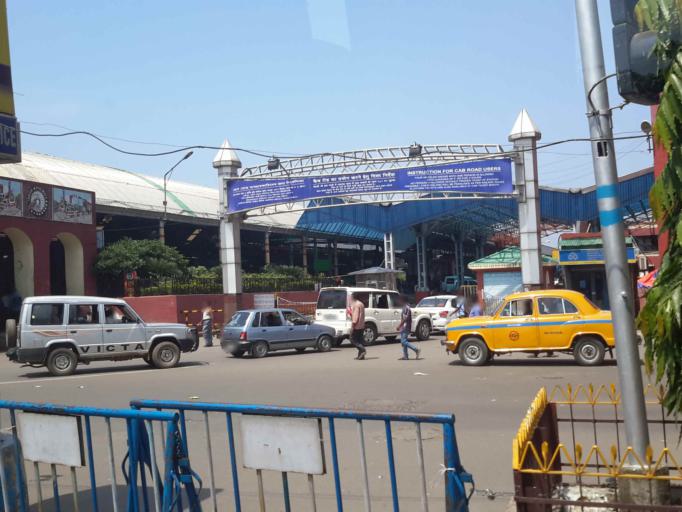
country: IN
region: West Bengal
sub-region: Kolkata
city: Bara Bazar
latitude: 22.5811
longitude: 88.3424
